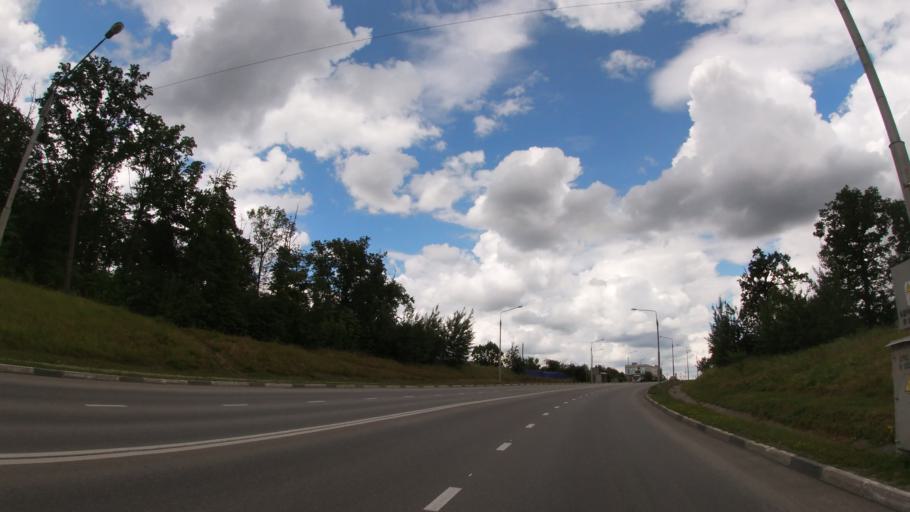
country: RU
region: Belgorod
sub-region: Belgorodskiy Rayon
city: Belgorod
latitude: 50.6242
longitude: 36.6114
